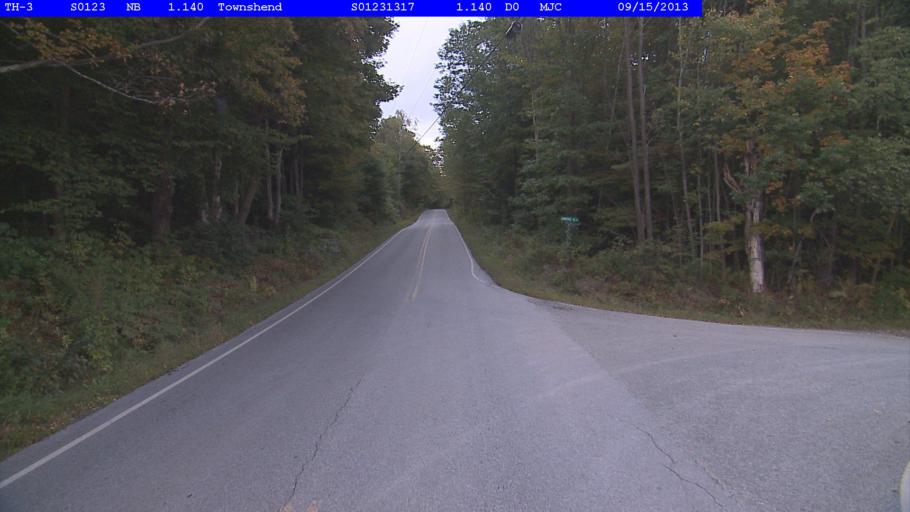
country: US
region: Vermont
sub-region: Windham County
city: Newfane
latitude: 43.0992
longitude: -72.7096
